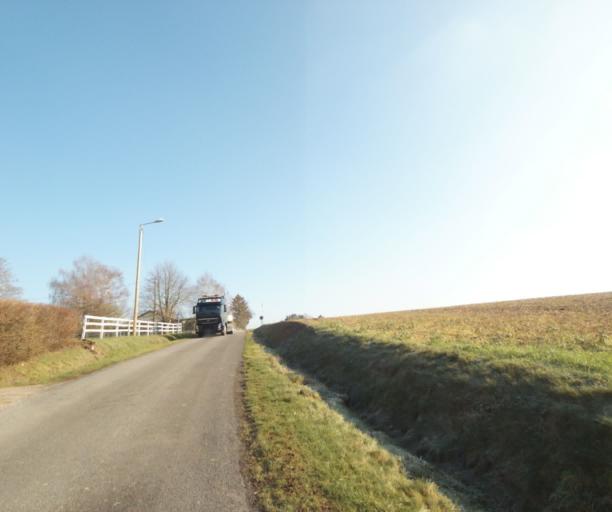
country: FR
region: Champagne-Ardenne
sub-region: Departement de la Haute-Marne
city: Wassy
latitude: 48.5227
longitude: 4.9914
